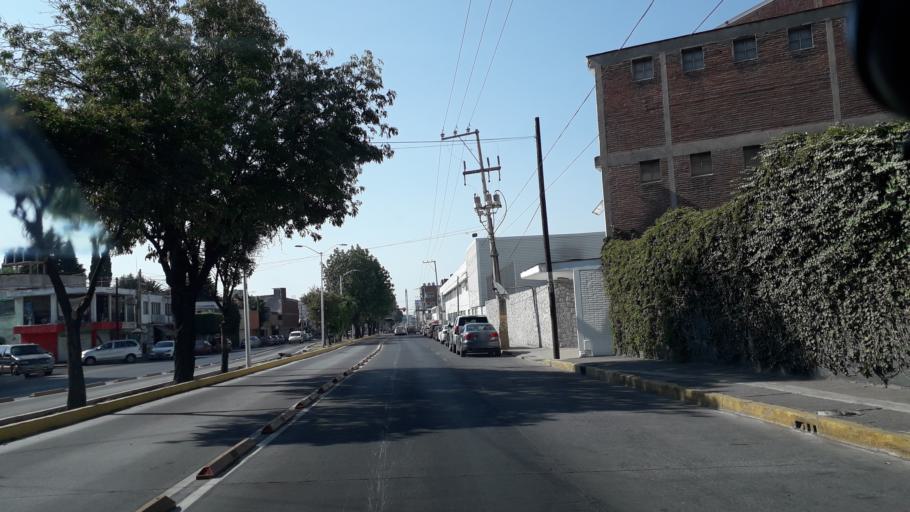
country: MX
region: Puebla
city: Puebla
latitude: 19.0314
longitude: -98.2157
